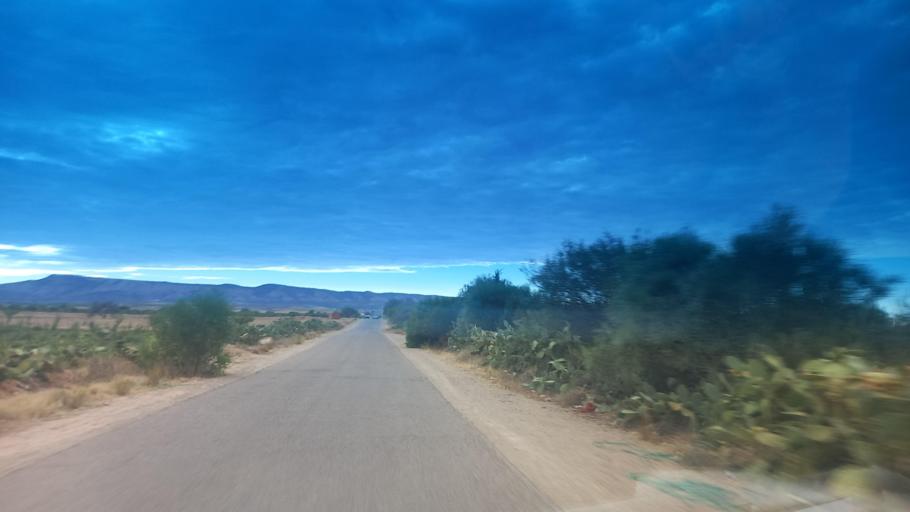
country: TN
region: Al Qasrayn
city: Sbiba
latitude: 35.3674
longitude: 9.0816
